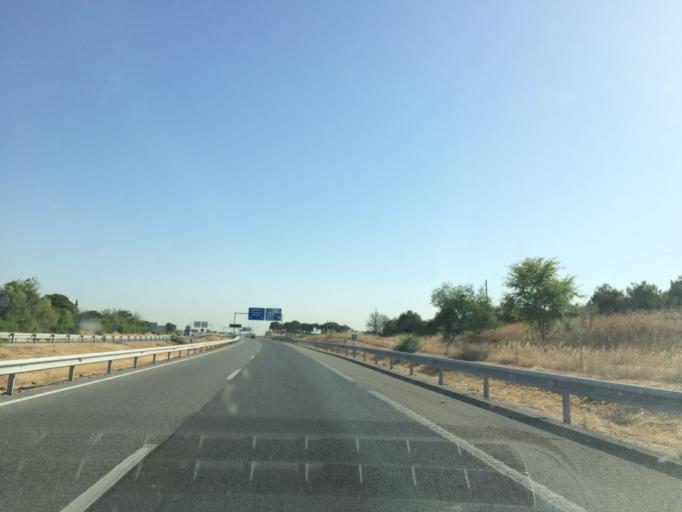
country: ES
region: Madrid
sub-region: Provincia de Madrid
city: Navalcarnero
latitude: 40.2540
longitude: -4.0500
